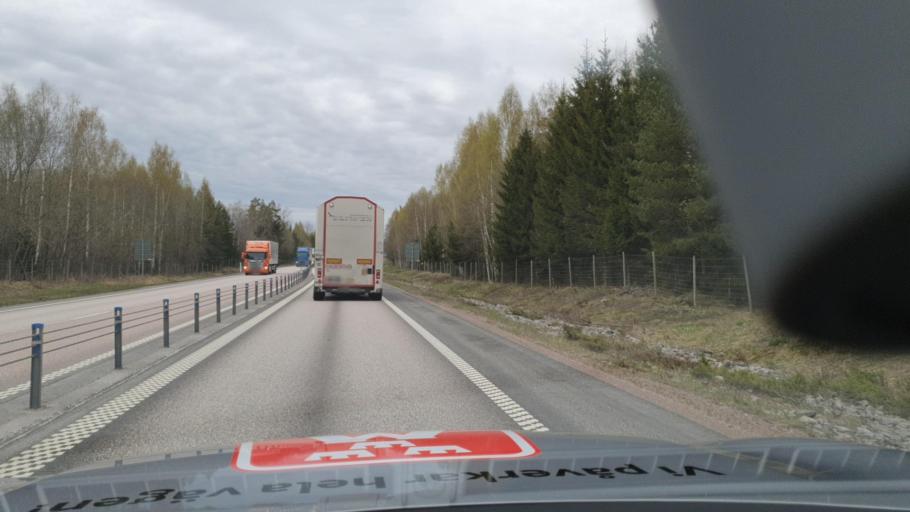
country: SE
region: Gaevleborg
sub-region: Gavle Kommun
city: Gavle
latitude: 60.7662
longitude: 17.0768
